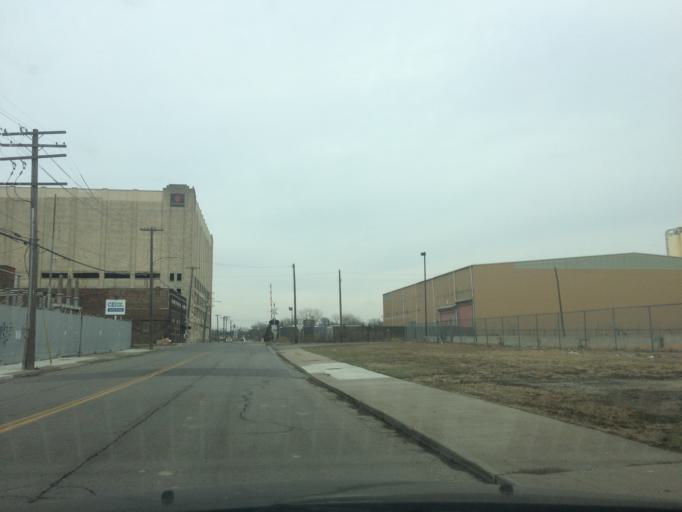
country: US
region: Michigan
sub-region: Wayne County
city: Hamtramck
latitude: 42.3674
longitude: -83.0503
